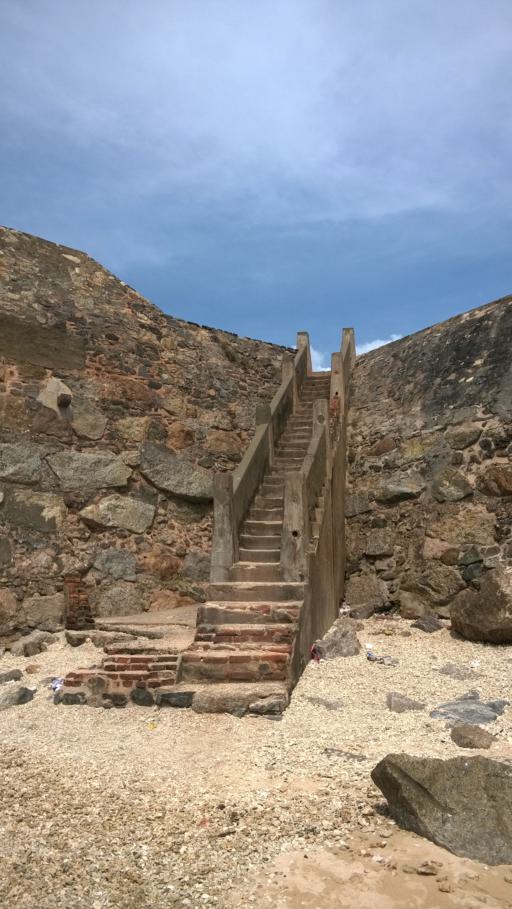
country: LK
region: Southern
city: Galle
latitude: 6.0249
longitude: 80.2163
